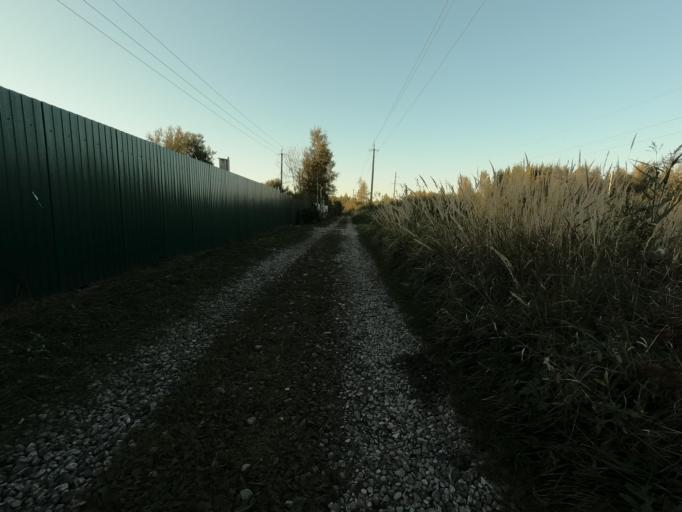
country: RU
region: Leningrad
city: Nikol'skoye
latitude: 59.7100
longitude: 30.7977
